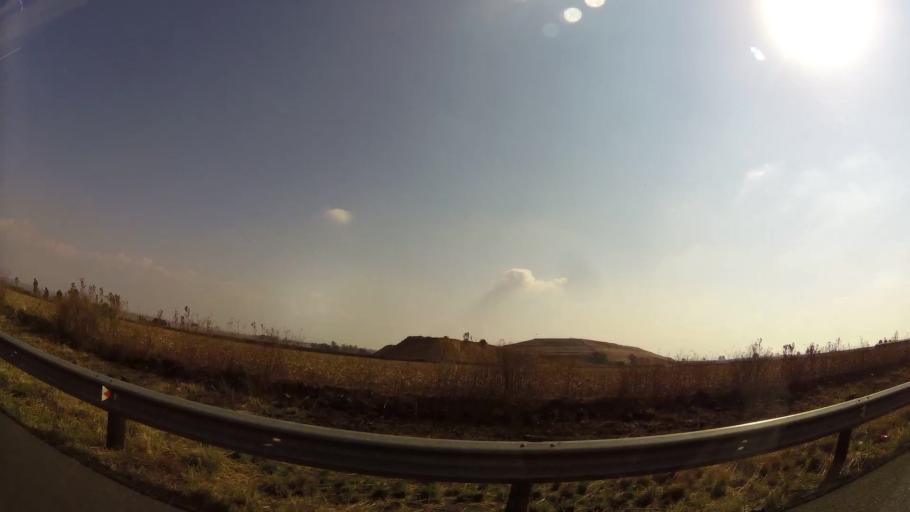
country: ZA
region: Gauteng
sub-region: Ekurhuleni Metropolitan Municipality
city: Springs
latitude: -26.1544
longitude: 28.5244
